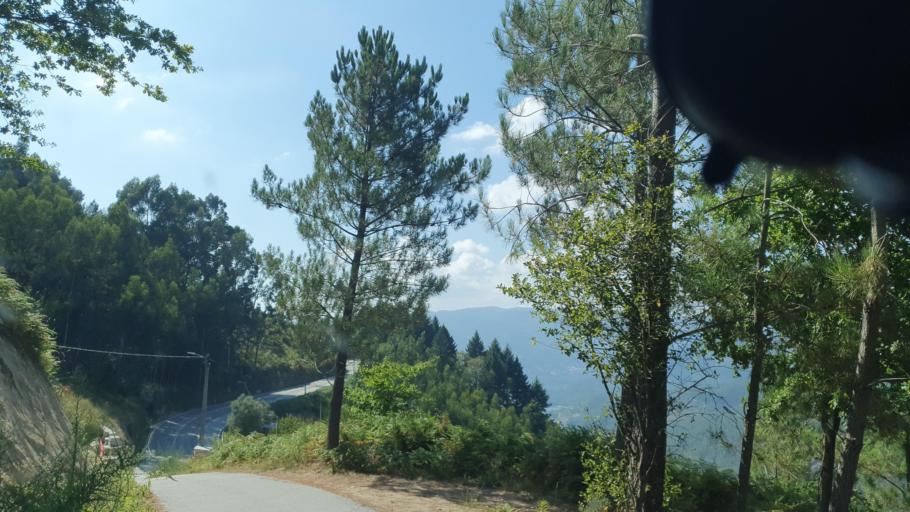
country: PT
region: Braga
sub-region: Vieira do Minho
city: Vieira do Minho
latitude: 41.6755
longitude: -8.1357
